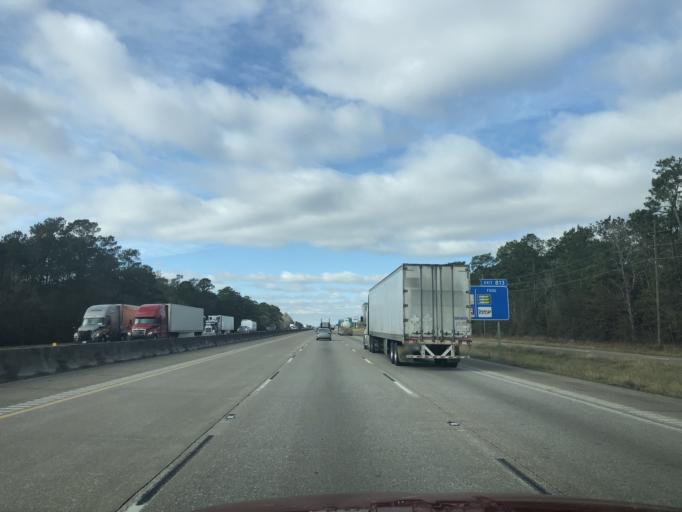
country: US
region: Texas
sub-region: Chambers County
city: Anahuac
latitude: 29.8395
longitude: -94.6323
